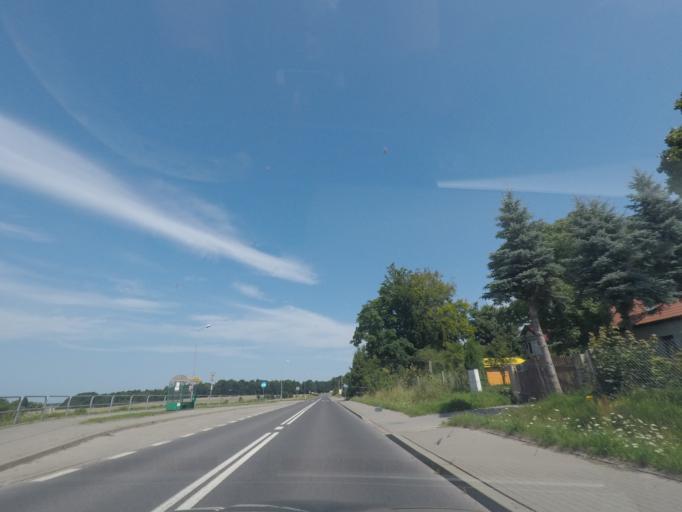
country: PL
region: West Pomeranian Voivodeship
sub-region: Powiat koszalinski
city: Sianow
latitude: 54.2664
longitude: 16.2675
